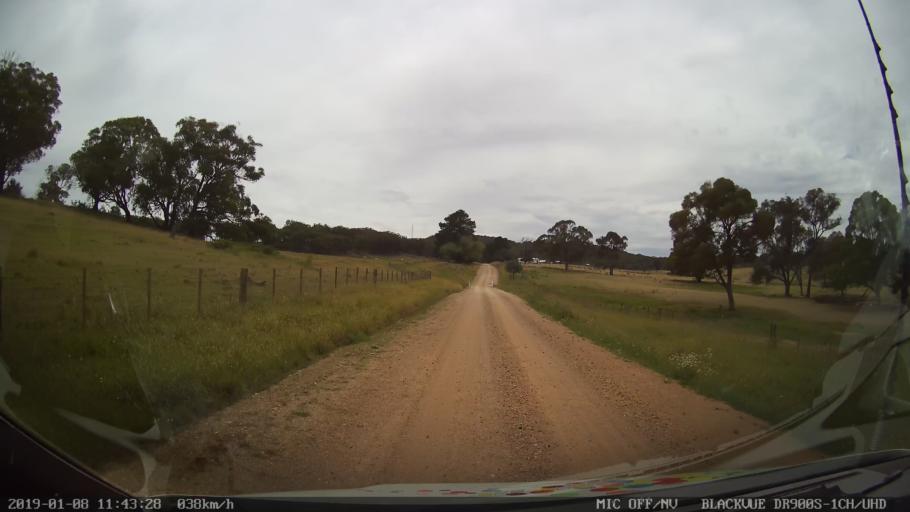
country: AU
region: New South Wales
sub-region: Armidale Dumaresq
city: Armidale
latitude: -30.3810
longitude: 151.5822
